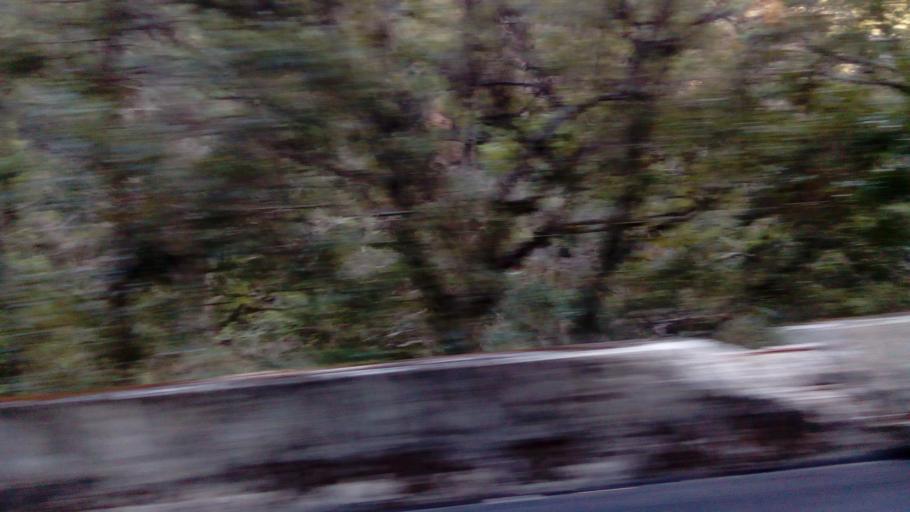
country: TW
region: Taiwan
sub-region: Hualien
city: Hualian
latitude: 24.3442
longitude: 121.3104
